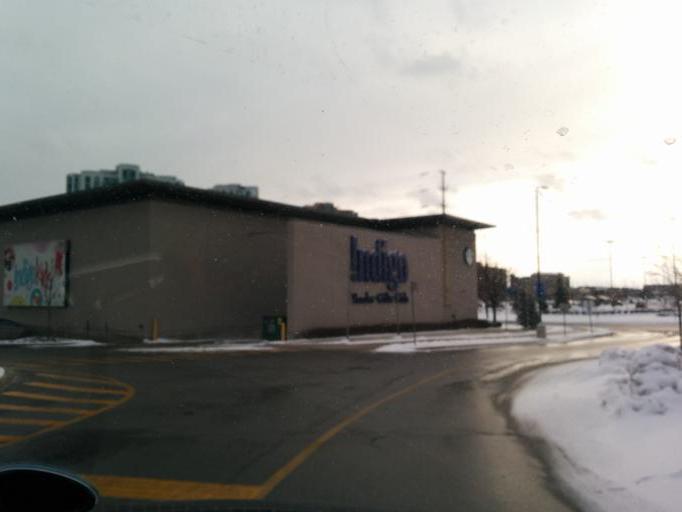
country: CA
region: Ontario
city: Mississauga
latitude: 43.5553
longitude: -79.7127
